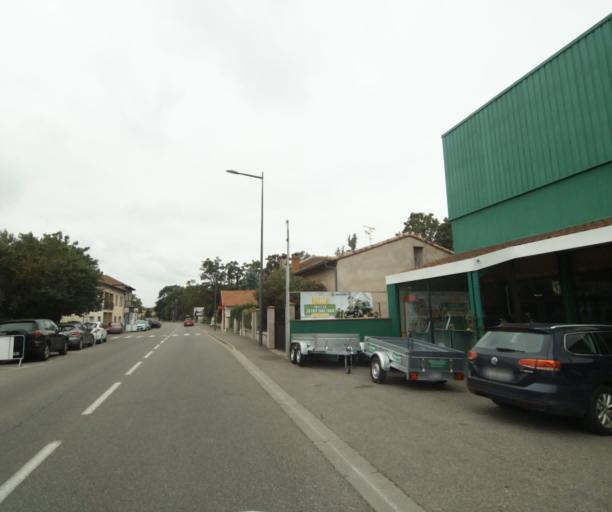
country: FR
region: Midi-Pyrenees
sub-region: Departement du Tarn-et-Garonne
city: Montauban
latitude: 44.0117
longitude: 1.3542
